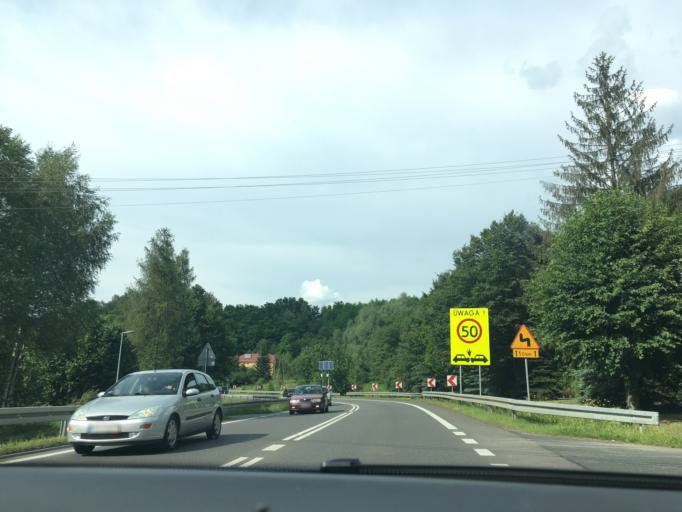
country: PL
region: Subcarpathian Voivodeship
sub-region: Powiat strzyzowski
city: Babica
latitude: 49.9206
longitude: 21.8795
